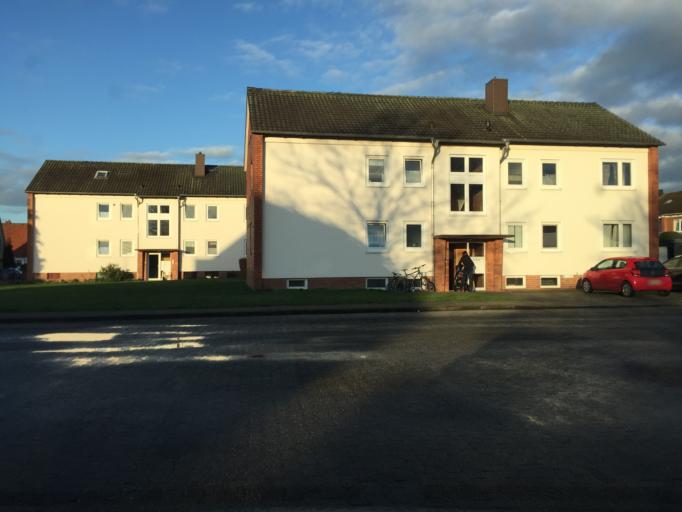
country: DE
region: Lower Saxony
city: Sulingen
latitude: 52.6865
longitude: 8.8217
